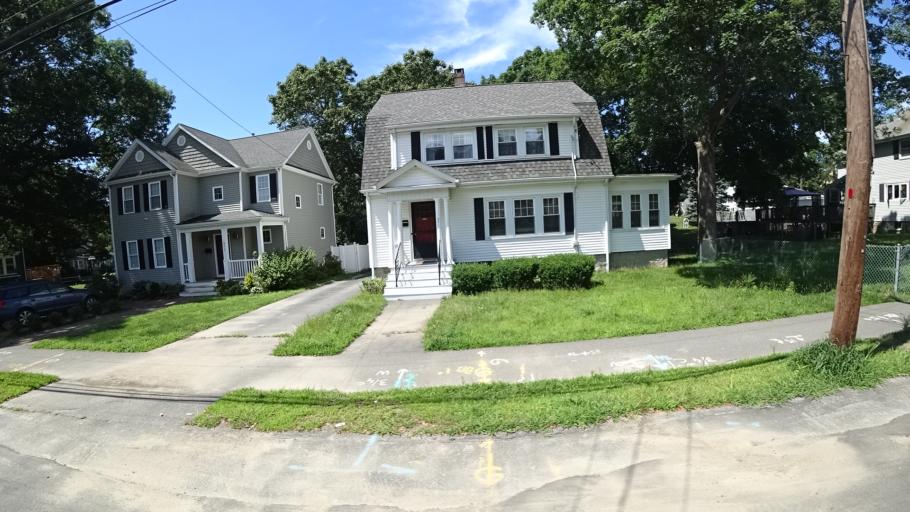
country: US
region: Massachusetts
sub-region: Norfolk County
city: Dedham
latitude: 42.2365
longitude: -71.1583
